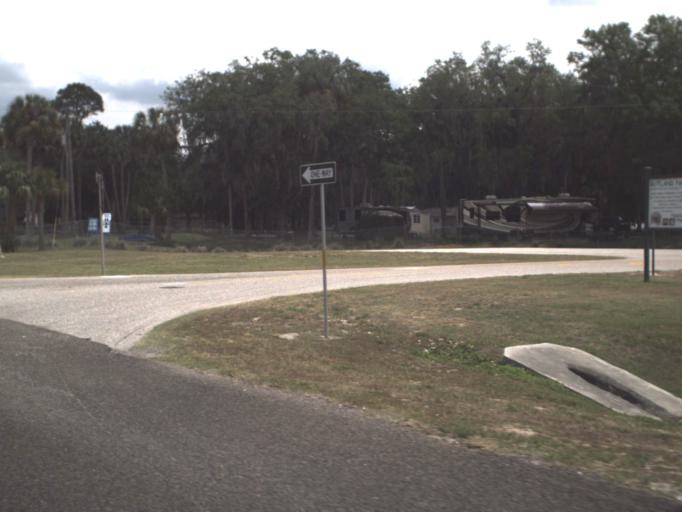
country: US
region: Florida
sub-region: Citrus County
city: Inverness
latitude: 28.8528
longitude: -82.2140
